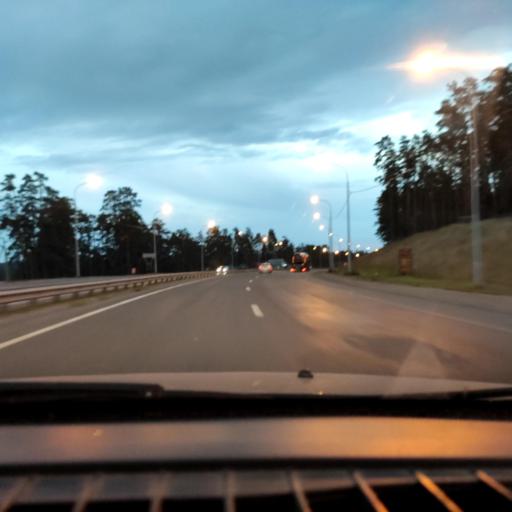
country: RU
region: Samara
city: Zhigulevsk
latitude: 53.5399
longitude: 49.5161
